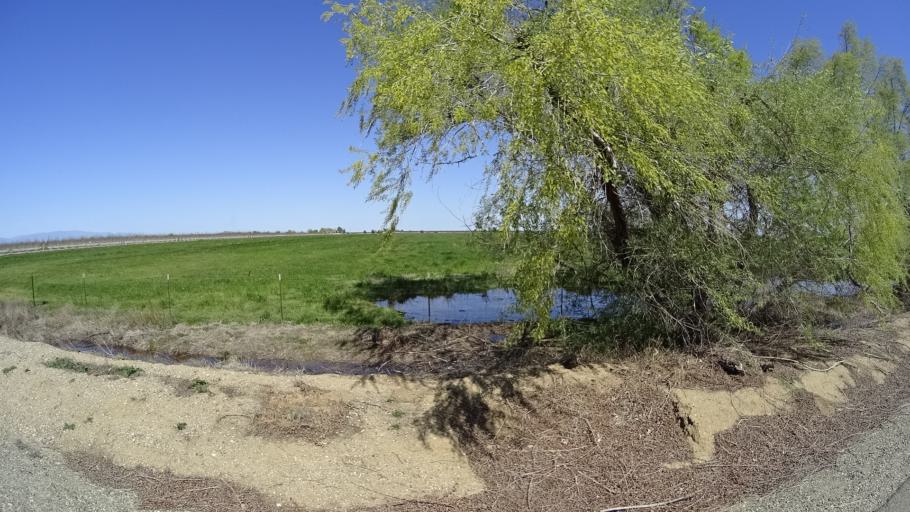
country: US
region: California
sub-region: Glenn County
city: Willows
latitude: 39.6247
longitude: -122.2516
